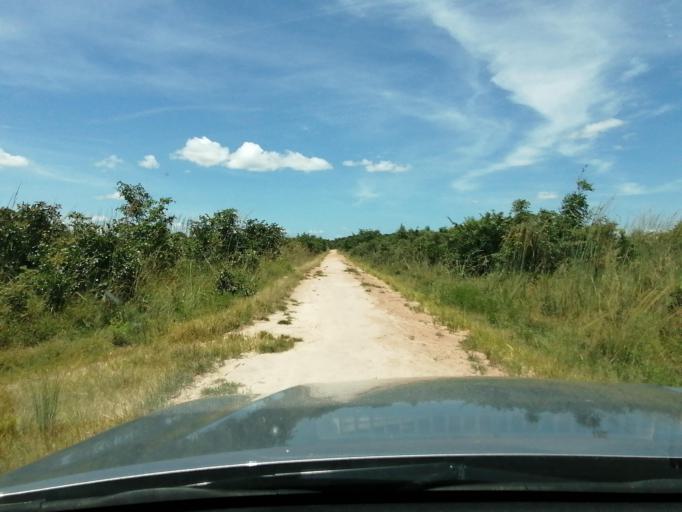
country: ZM
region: Central
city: Chibombo
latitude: -15.1005
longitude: 27.8489
